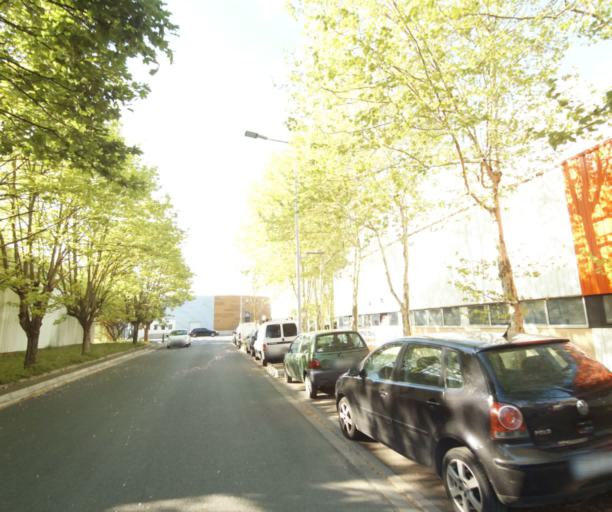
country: FR
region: Ile-de-France
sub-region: Departement de Seine-et-Marne
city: Torcy
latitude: 48.8432
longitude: 2.6568
